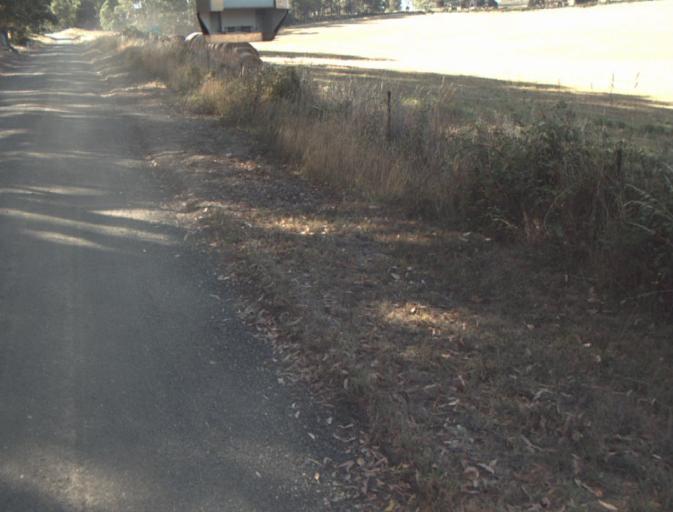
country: AU
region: Tasmania
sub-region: Dorset
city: Bridport
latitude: -41.1499
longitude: 147.2251
